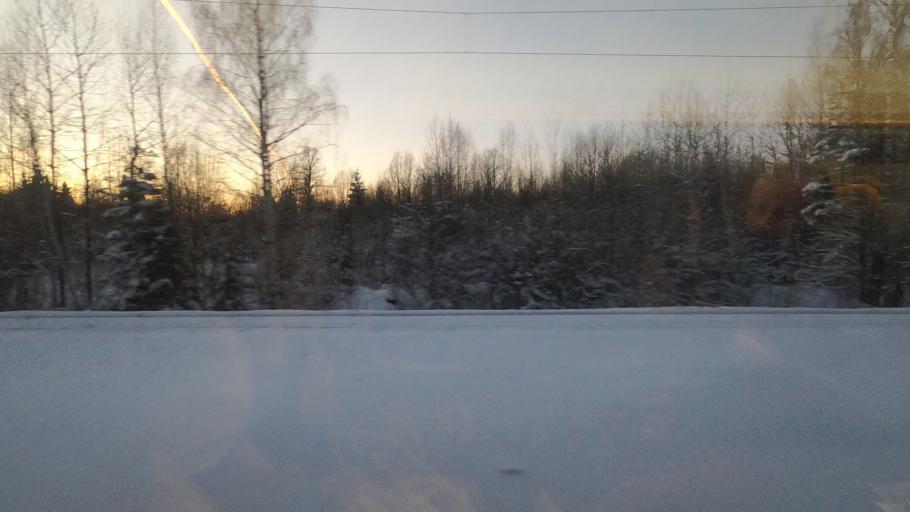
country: RU
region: Moskovskaya
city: Lugovaya
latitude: 56.0339
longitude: 37.4884
